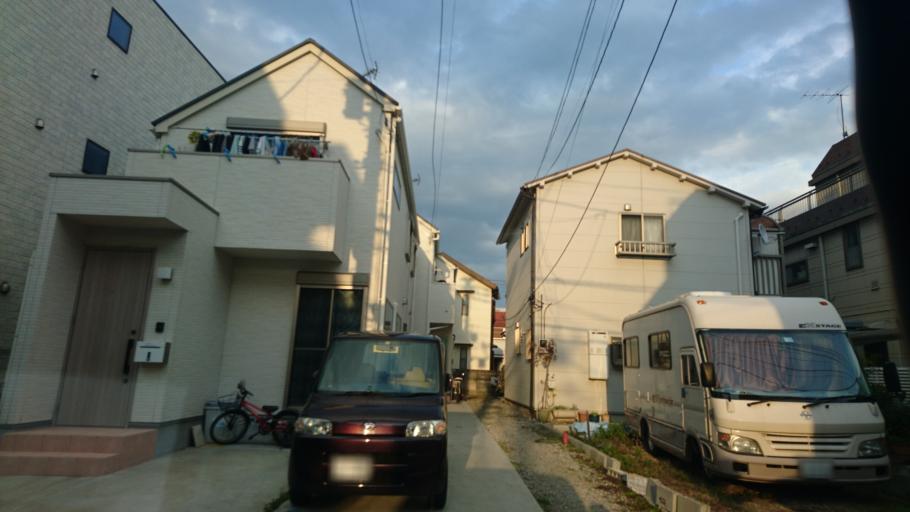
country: JP
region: Kanagawa
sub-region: Kawasaki-shi
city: Kawasaki
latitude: 35.5770
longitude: 139.7321
